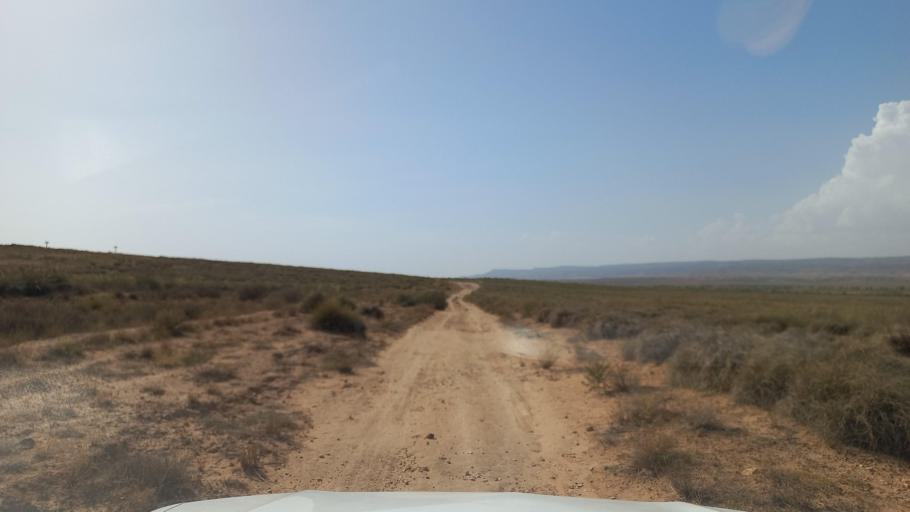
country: TN
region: Al Qasrayn
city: Kasserine
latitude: 35.2148
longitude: 8.9894
